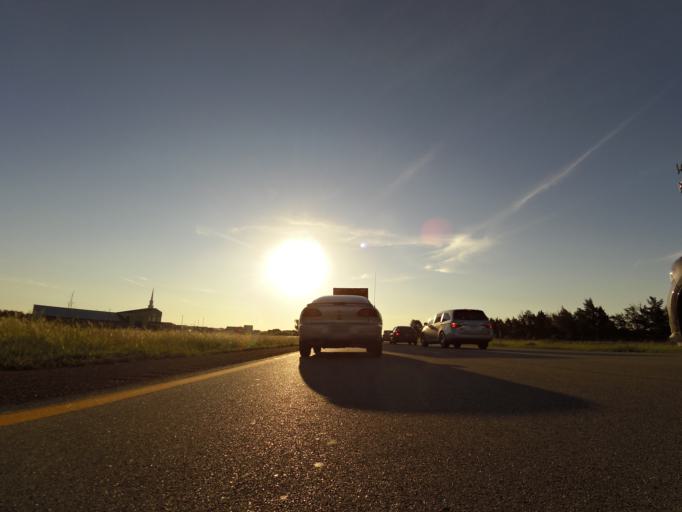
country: US
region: Kansas
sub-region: Sedgwick County
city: Maize
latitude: 37.7596
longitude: -97.4228
